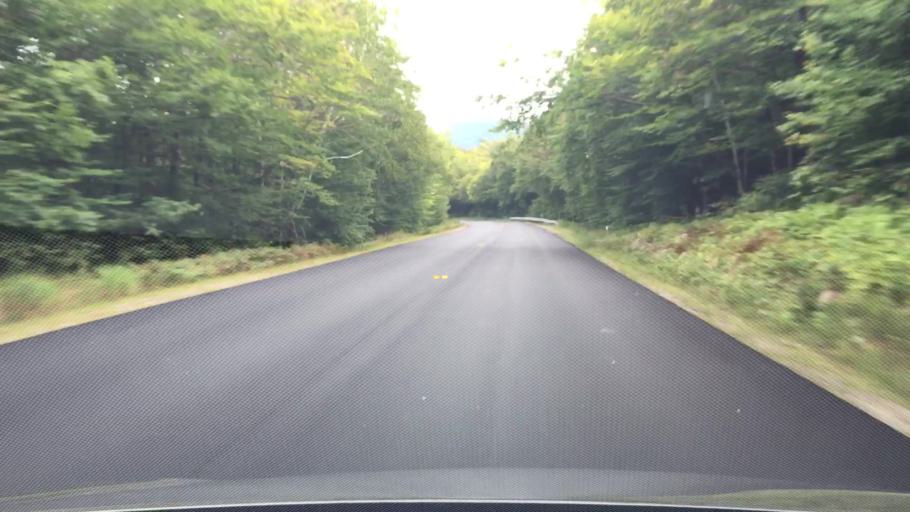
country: US
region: New Hampshire
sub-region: Carroll County
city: Sandwich
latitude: 44.0188
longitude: -71.4351
